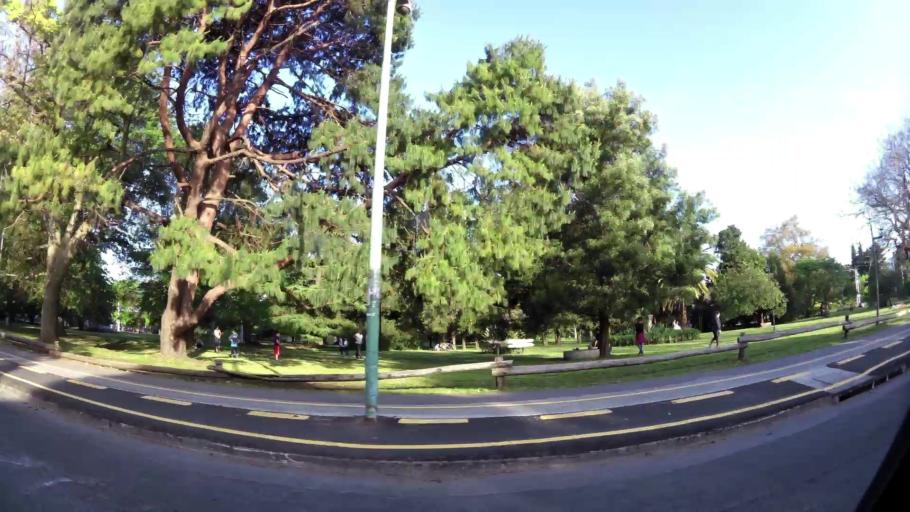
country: AR
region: Buenos Aires
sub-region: Partido de Quilmes
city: Quilmes
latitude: -34.7870
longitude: -58.2027
